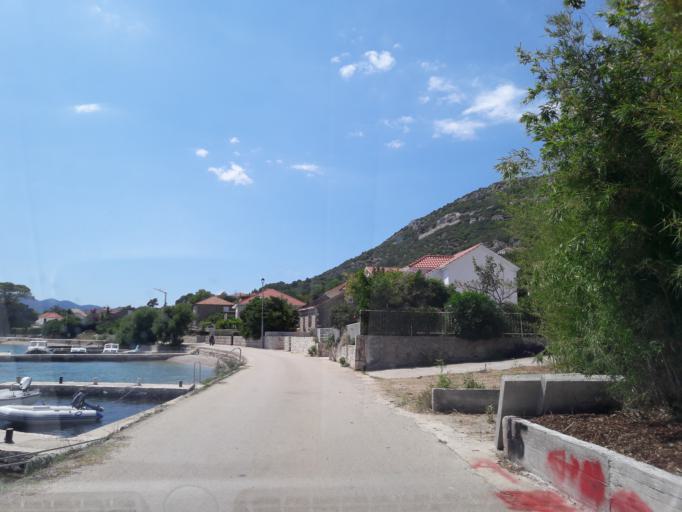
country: HR
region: Dubrovacko-Neretvanska
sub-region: Grad Korcula
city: Zrnovo
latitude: 42.9846
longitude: 17.0910
